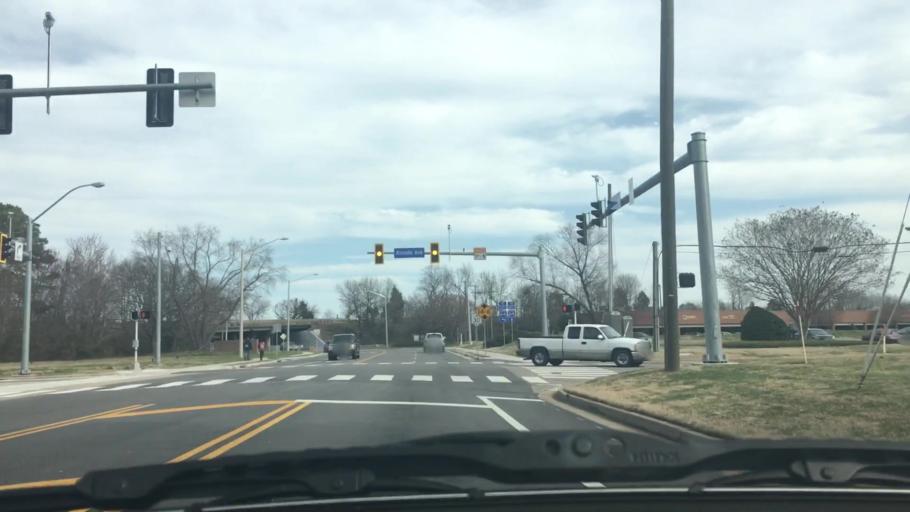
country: US
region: Virginia
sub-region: City of Norfolk
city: Norfolk
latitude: 36.8811
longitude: -76.2178
